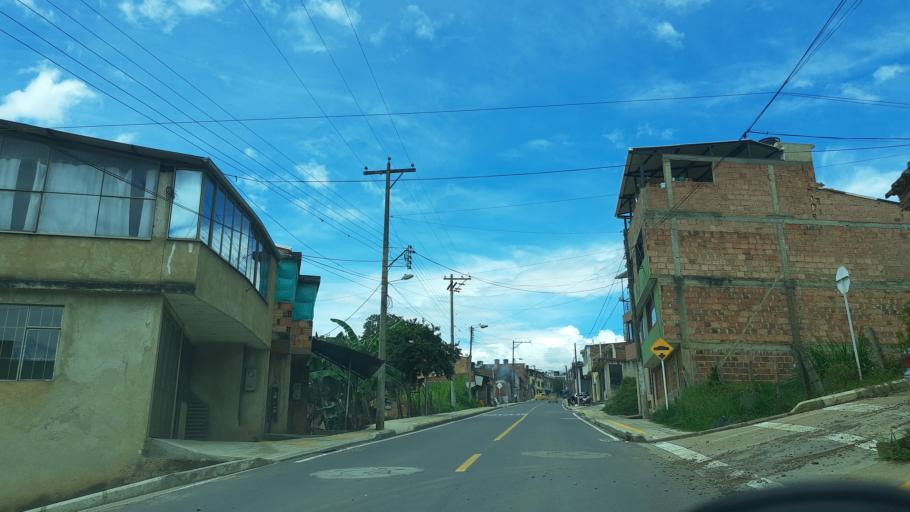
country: CO
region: Boyaca
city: Guateque
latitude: 5.0074
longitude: -73.4683
